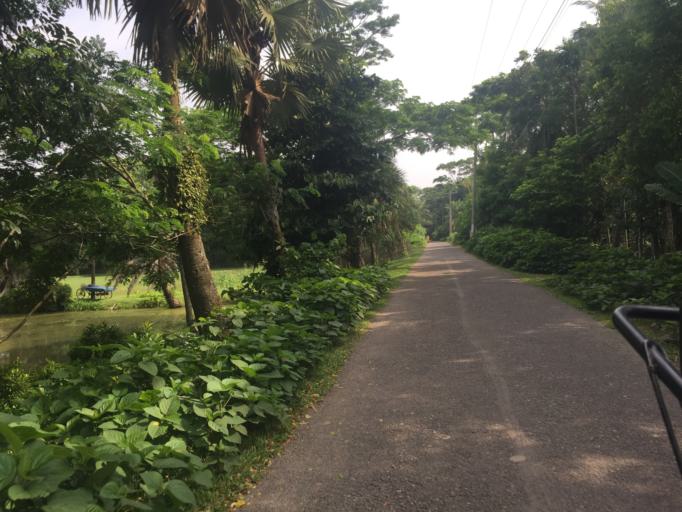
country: BD
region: Barisal
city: Mathba
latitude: 22.2221
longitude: 89.9161
